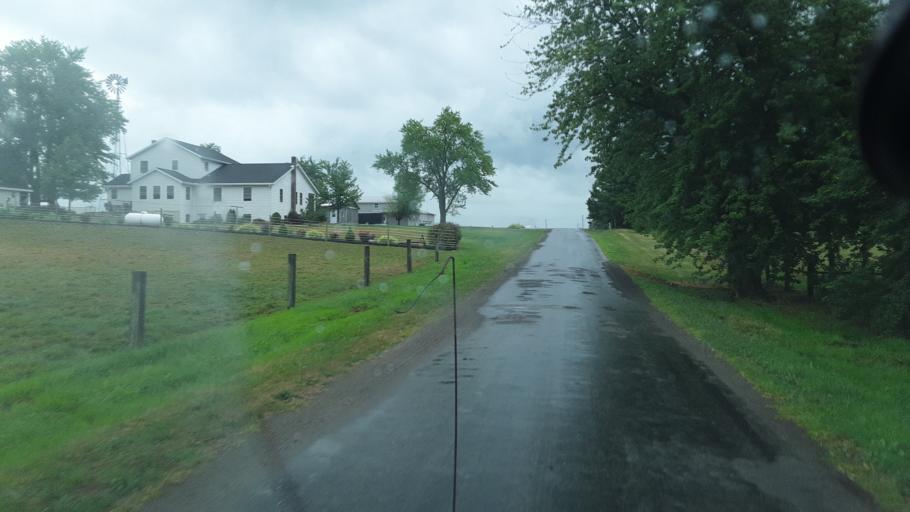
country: US
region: Indiana
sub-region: Steuben County
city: Hamilton
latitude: 41.5708
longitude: -84.7923
